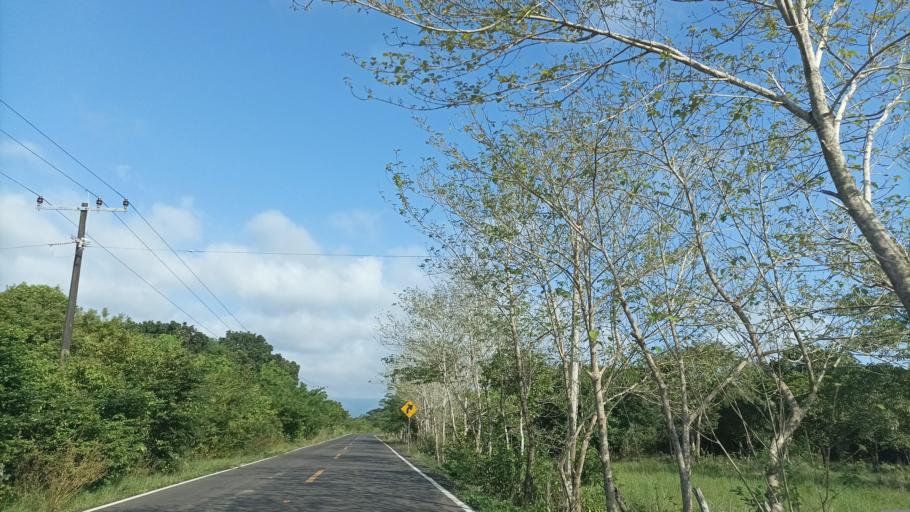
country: MX
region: Veracruz
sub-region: Chinameca
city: Chacalapa
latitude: 18.1544
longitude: -94.6567
